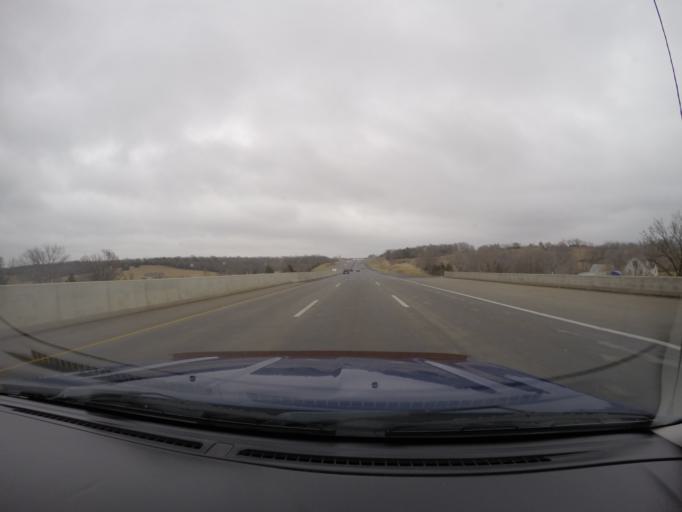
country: US
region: Kansas
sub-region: Shawnee County
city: Topeka
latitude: 39.0156
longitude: -95.4828
